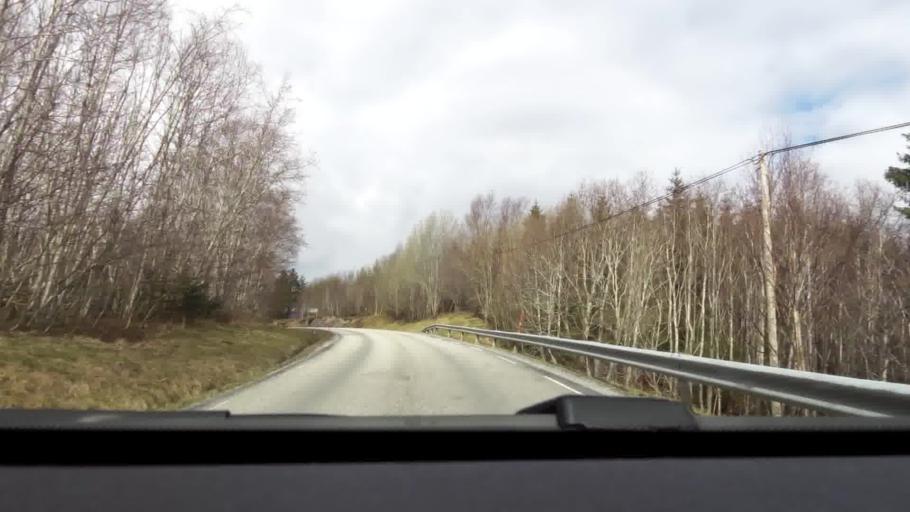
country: NO
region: More og Romsdal
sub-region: Gjemnes
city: Batnfjordsora
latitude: 62.9664
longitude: 7.7408
